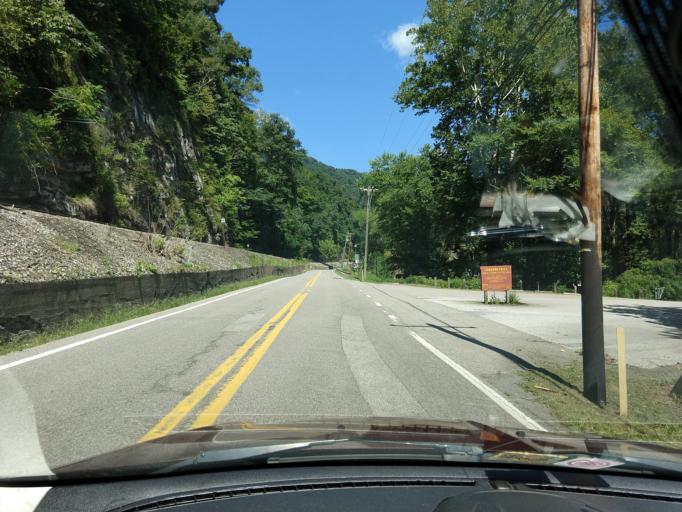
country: US
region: West Virginia
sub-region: Fayette County
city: Ansted
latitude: 38.1452
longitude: -81.2132
